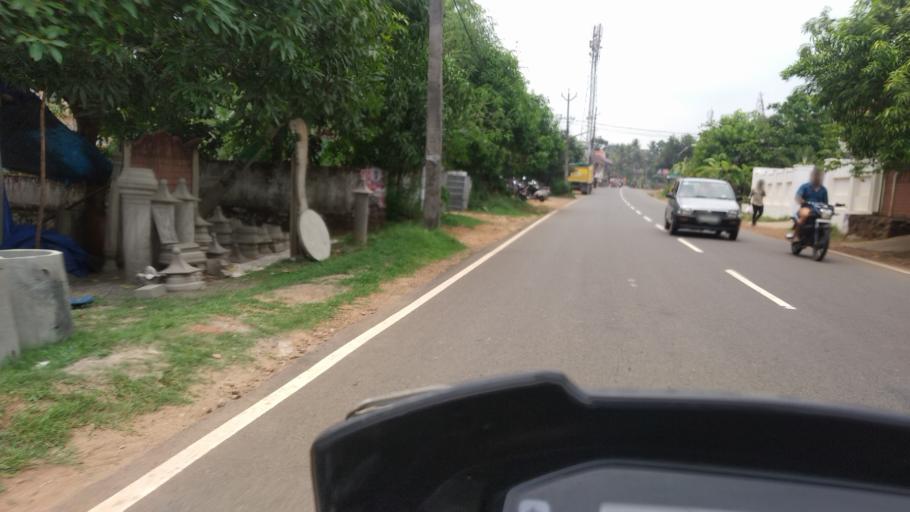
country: IN
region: Kerala
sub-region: Ernakulam
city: Aluva
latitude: 10.1560
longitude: 76.3298
